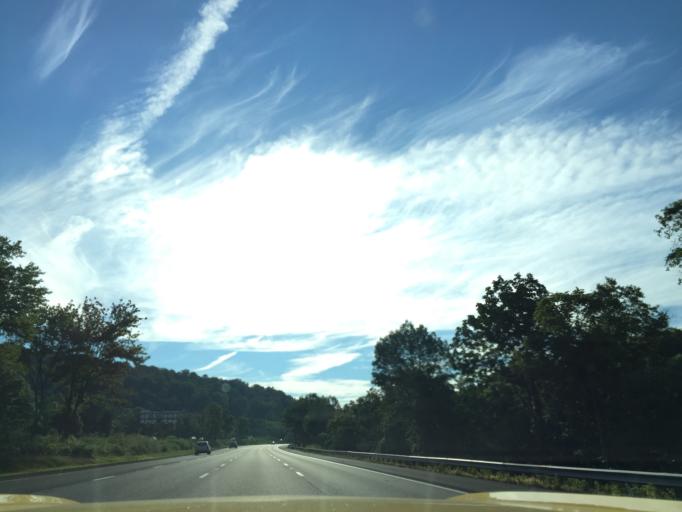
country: US
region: New Jersey
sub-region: Somerset County
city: Bedminster
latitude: 40.6436
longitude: -74.6309
